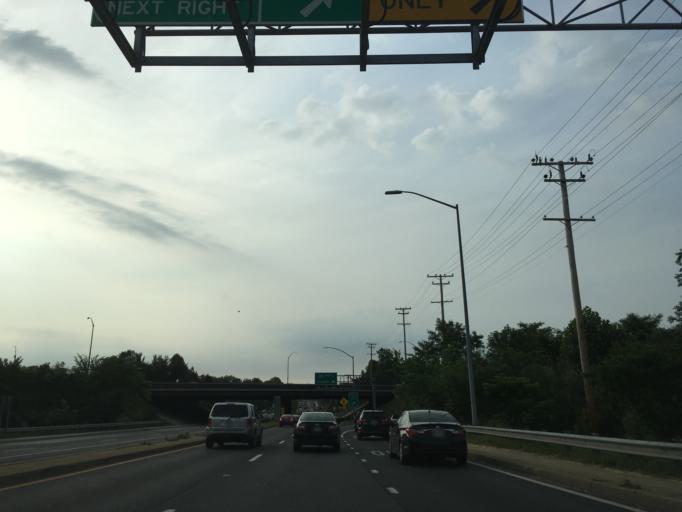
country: US
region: Maryland
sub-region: Baltimore County
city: Milford Mill
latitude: 39.3498
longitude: -76.7473
